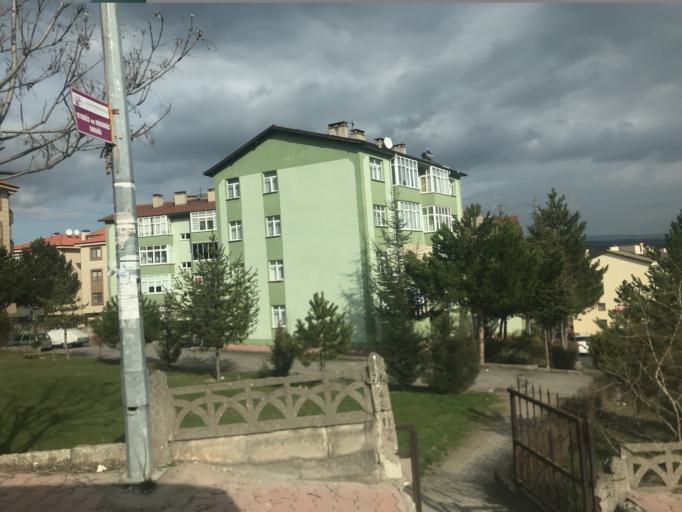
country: TR
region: Karabuk
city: Safranbolu
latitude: 41.2549
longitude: 32.6823
